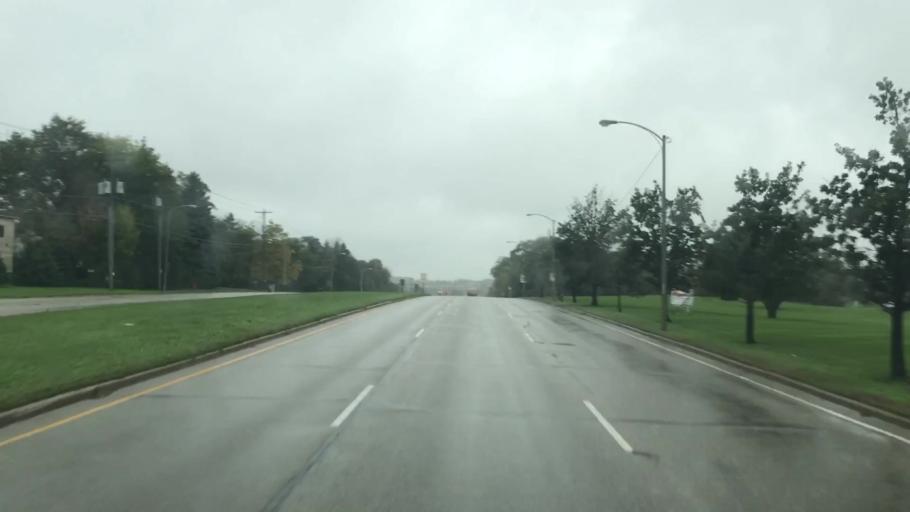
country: US
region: Wisconsin
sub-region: Waukesha County
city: Menomonee Falls
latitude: 43.1773
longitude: -88.0574
